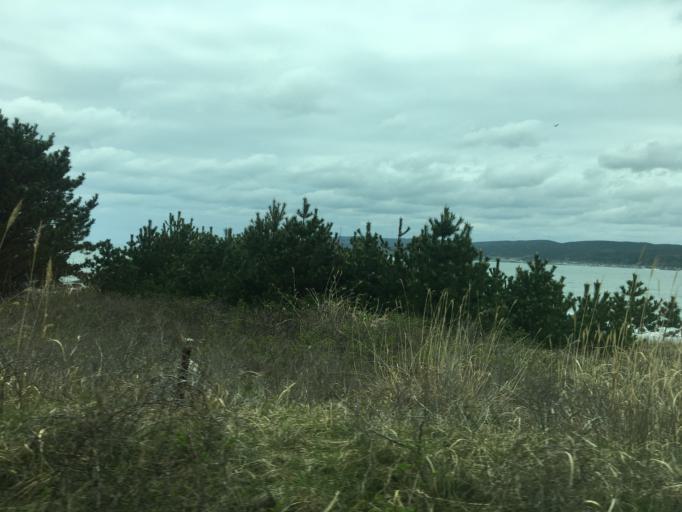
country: JP
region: Akita
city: Noshiromachi
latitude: 40.5612
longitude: 139.9327
